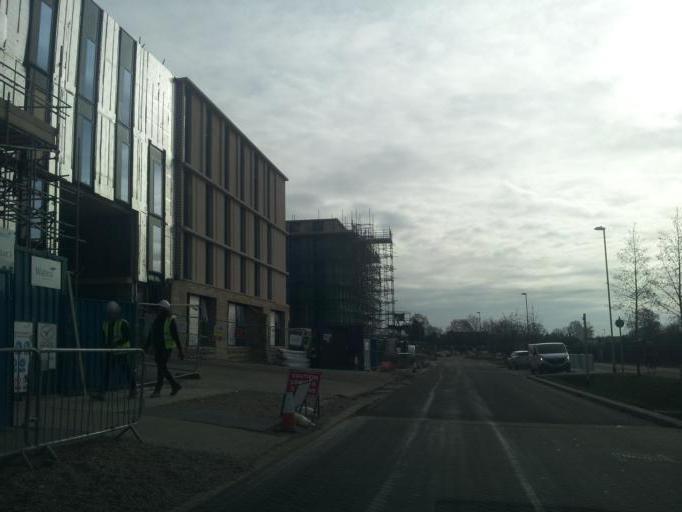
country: GB
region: England
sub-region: Cambridgeshire
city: Girton
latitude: 52.2186
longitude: 0.0844
